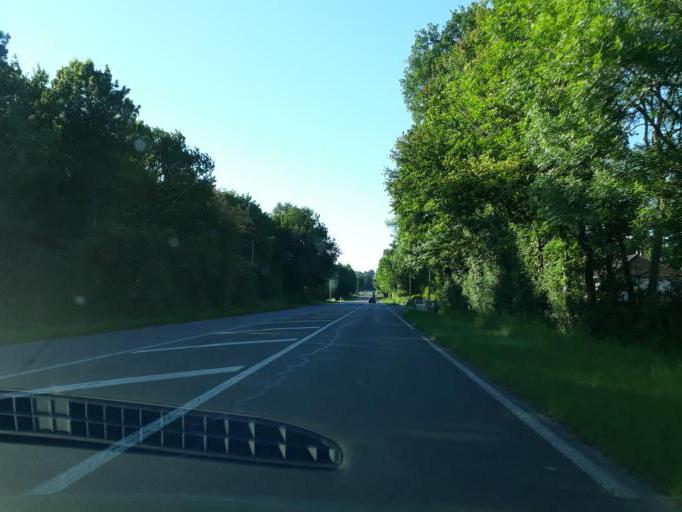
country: FR
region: Centre
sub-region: Departement du Cher
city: Lere
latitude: 47.4771
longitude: 2.9268
